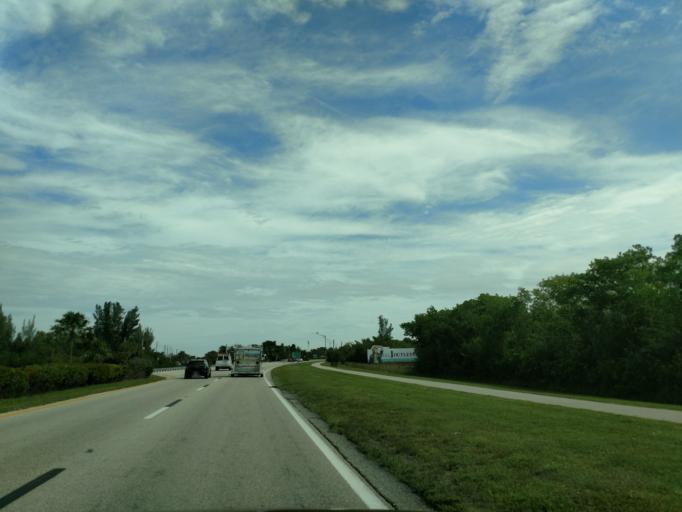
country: US
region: Florida
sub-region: Lee County
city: Punta Rassa
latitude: 26.4924
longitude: -81.9808
